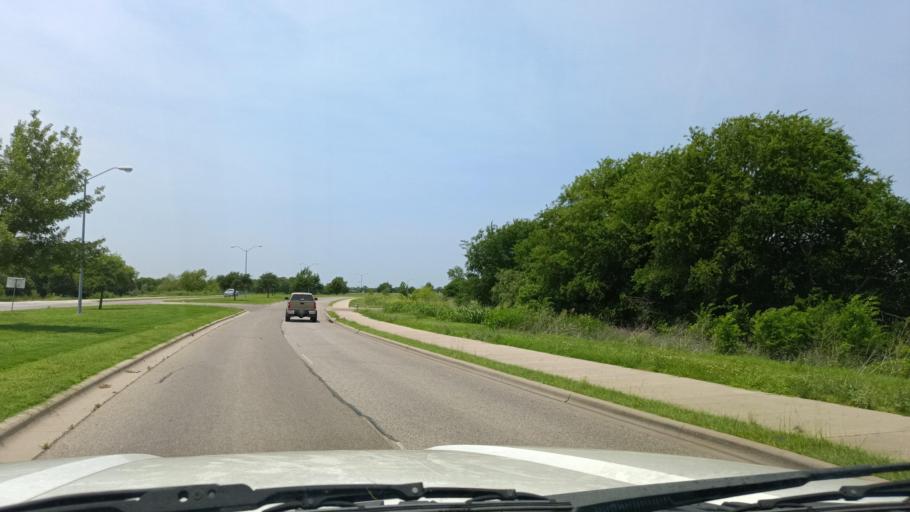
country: US
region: Texas
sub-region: Bell County
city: Temple
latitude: 31.1289
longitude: -97.4005
